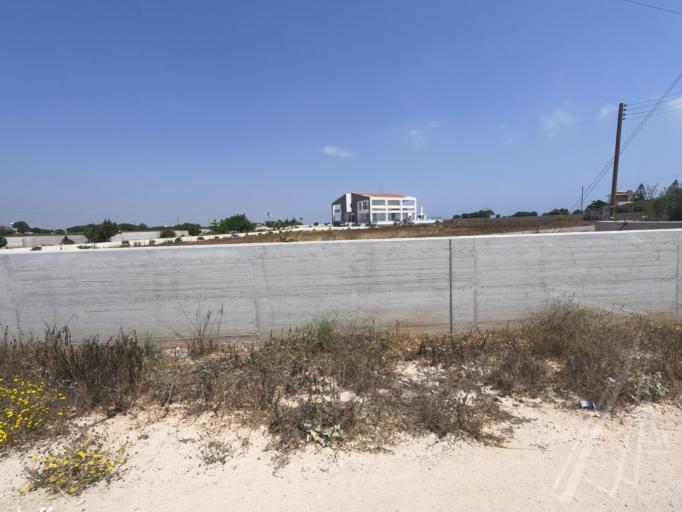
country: CY
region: Ammochostos
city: Ayia Napa
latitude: 35.0055
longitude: 34.0001
